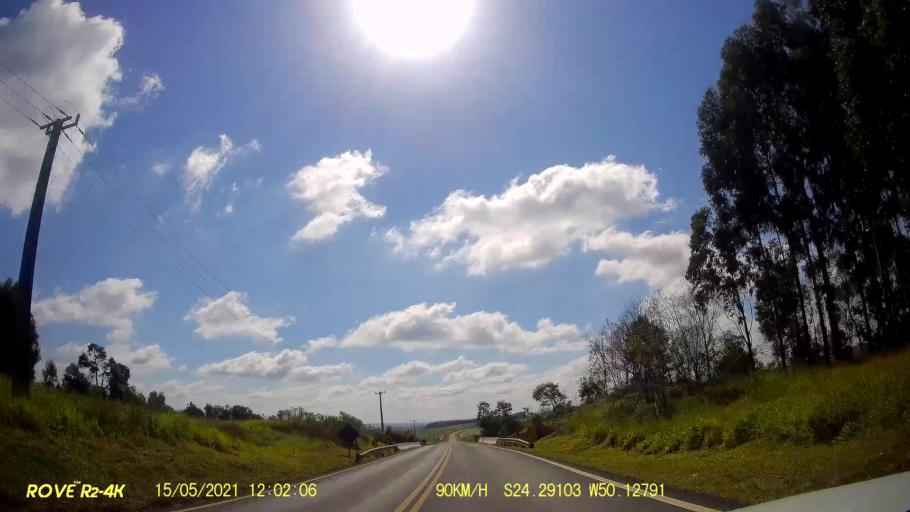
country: BR
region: Parana
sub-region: Pirai Do Sul
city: Pirai do Sul
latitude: -24.2910
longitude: -50.1282
